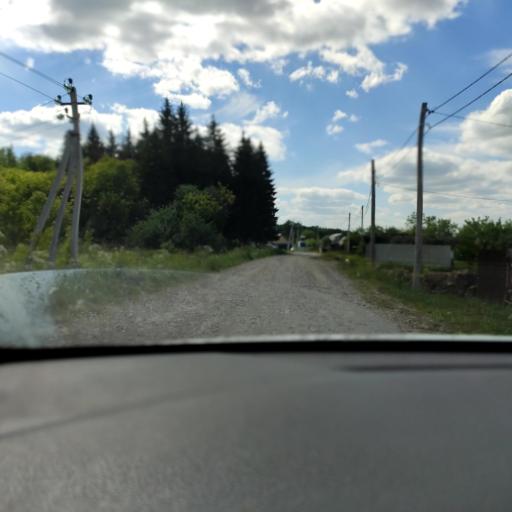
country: RU
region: Tatarstan
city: Vysokaya Gora
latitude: 55.9506
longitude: 49.2965
